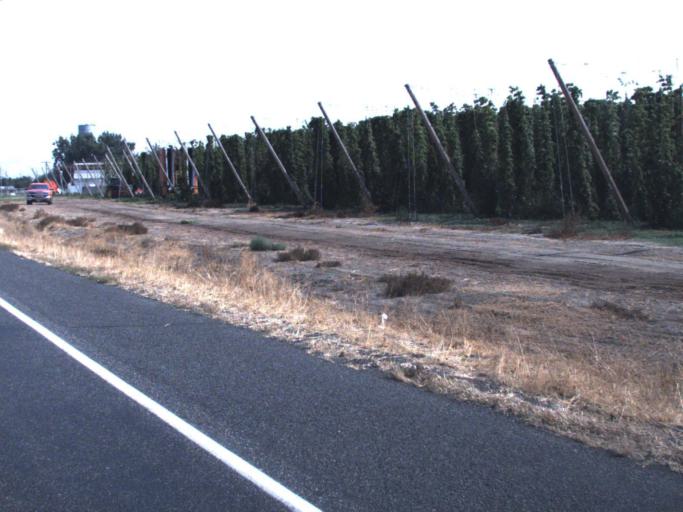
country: US
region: Washington
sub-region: Yakima County
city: Mabton
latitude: 46.2136
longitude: -120.0078
